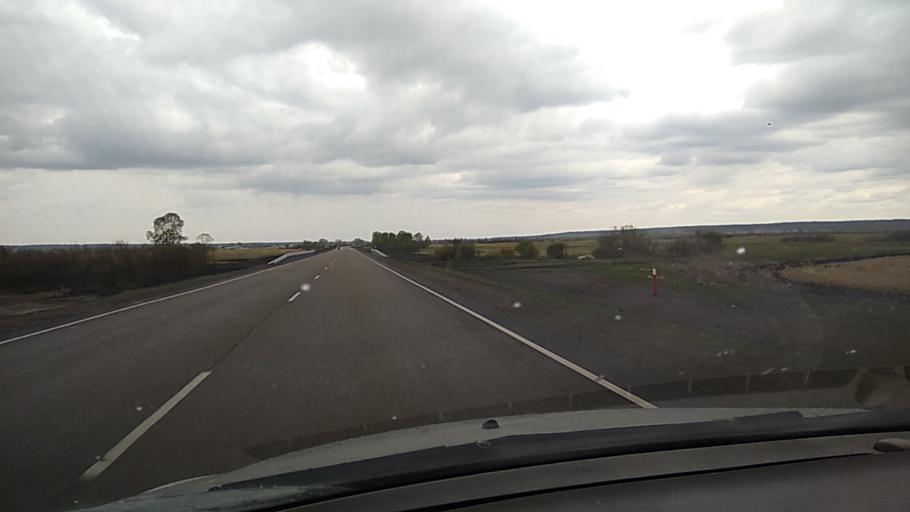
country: RU
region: Kurgan
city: Kataysk
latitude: 56.3016
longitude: 62.4999
